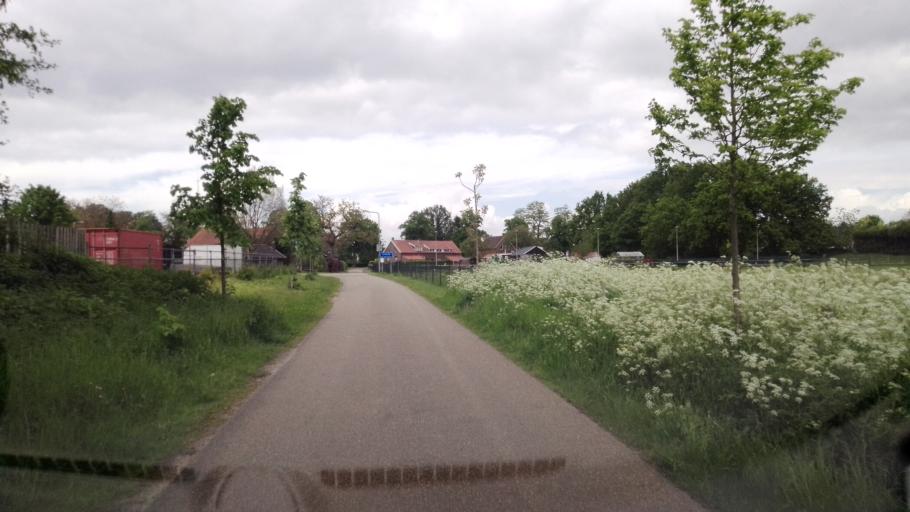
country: NL
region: Limburg
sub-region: Gemeente Venlo
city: Arcen
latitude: 51.4546
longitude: 6.1591
